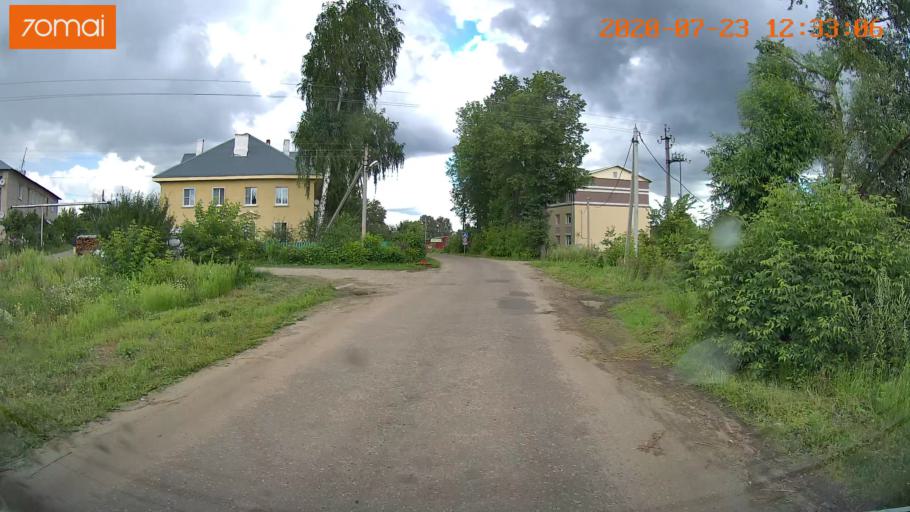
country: RU
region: Ivanovo
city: Bogorodskoye
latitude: 57.0480
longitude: 41.0072
